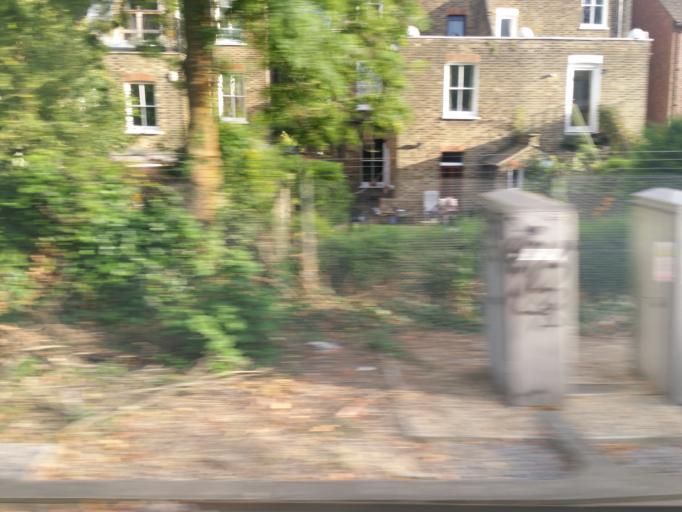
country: GB
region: England
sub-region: Greater London
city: Belsize Park
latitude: 51.5562
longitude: -0.1562
